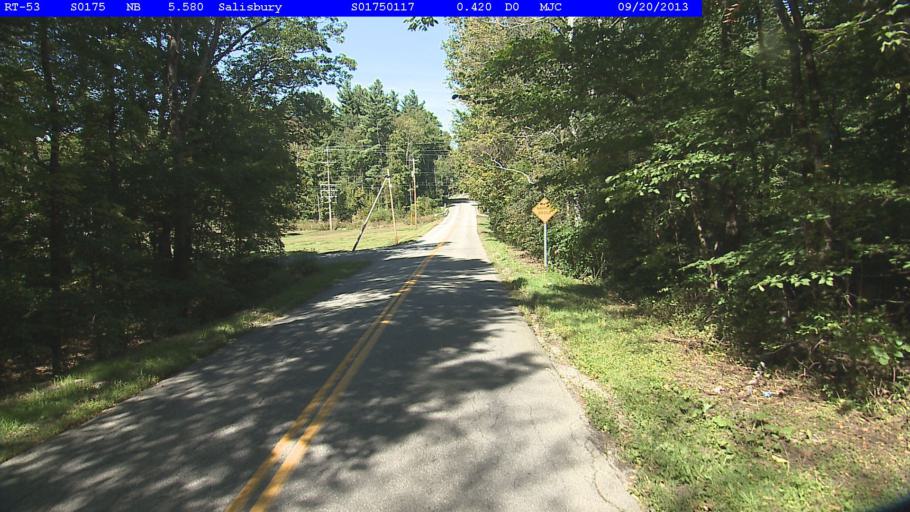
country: US
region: Vermont
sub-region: Rutland County
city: Brandon
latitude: 43.9037
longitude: -73.0651
